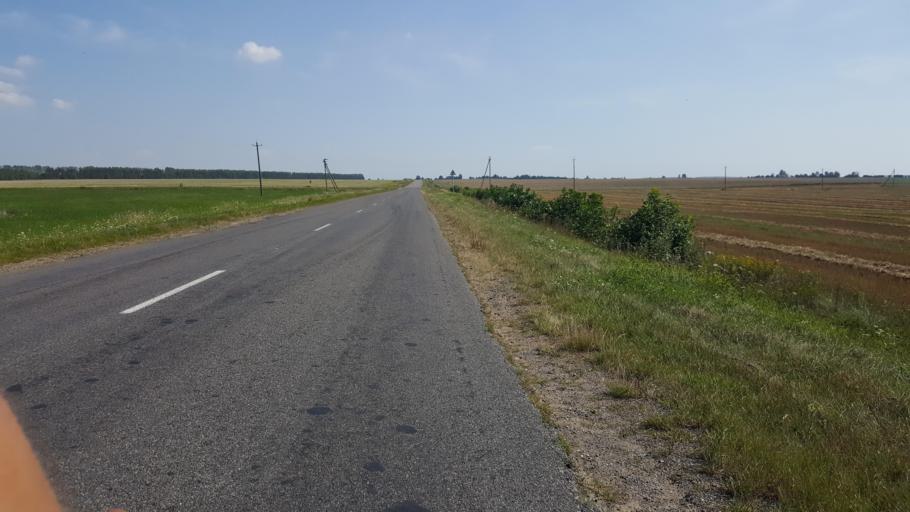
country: BY
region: Brest
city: Kamyanyets
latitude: 52.4616
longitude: 23.7199
